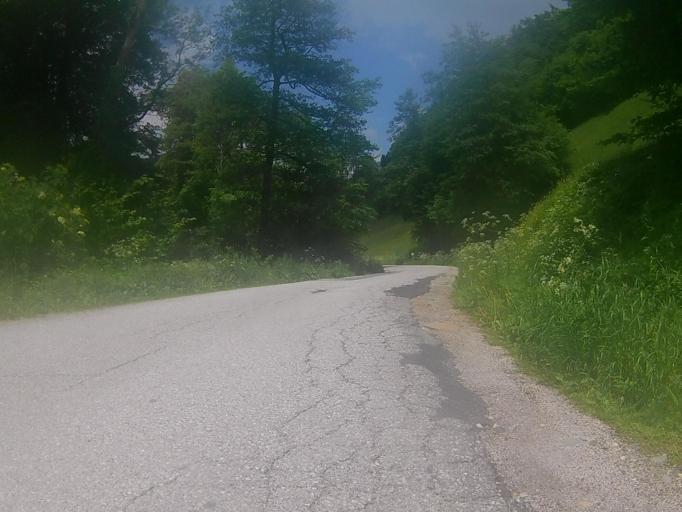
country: SI
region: Maribor
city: Bresternica
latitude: 46.6071
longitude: 15.5513
